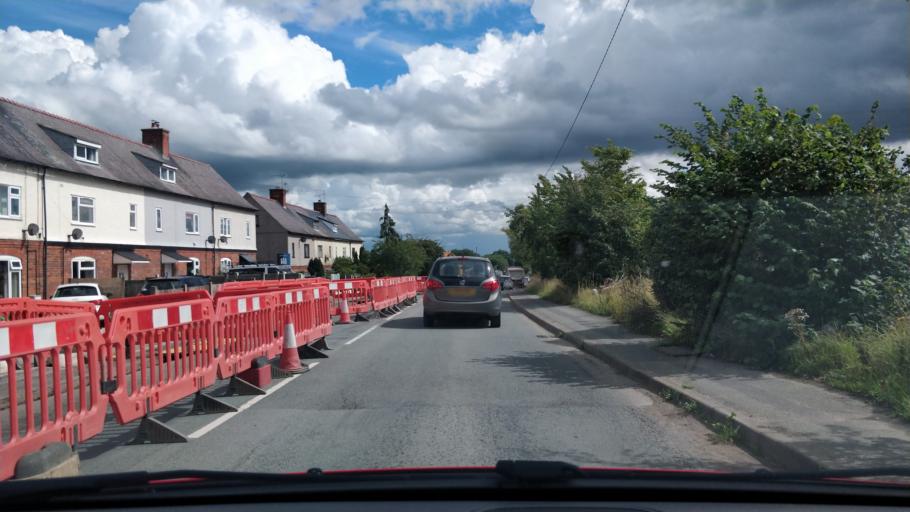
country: GB
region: Wales
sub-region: County of Flintshire
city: Hope
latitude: 53.1021
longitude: -3.0034
